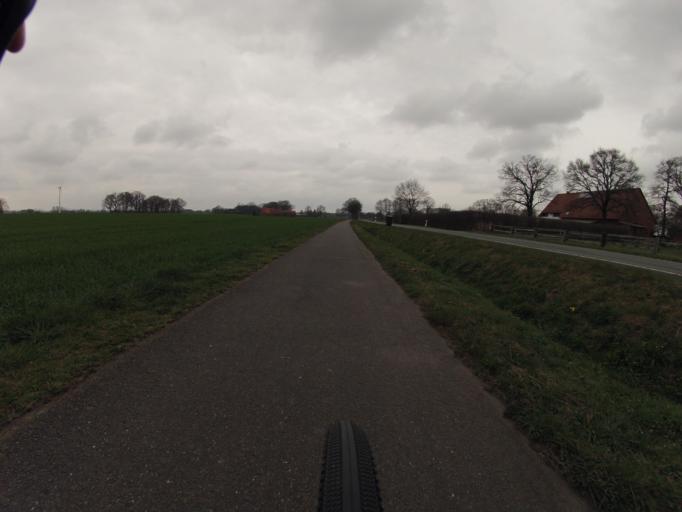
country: DE
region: North Rhine-Westphalia
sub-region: Regierungsbezirk Munster
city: Mettingen
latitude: 52.3446
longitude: 7.8088
